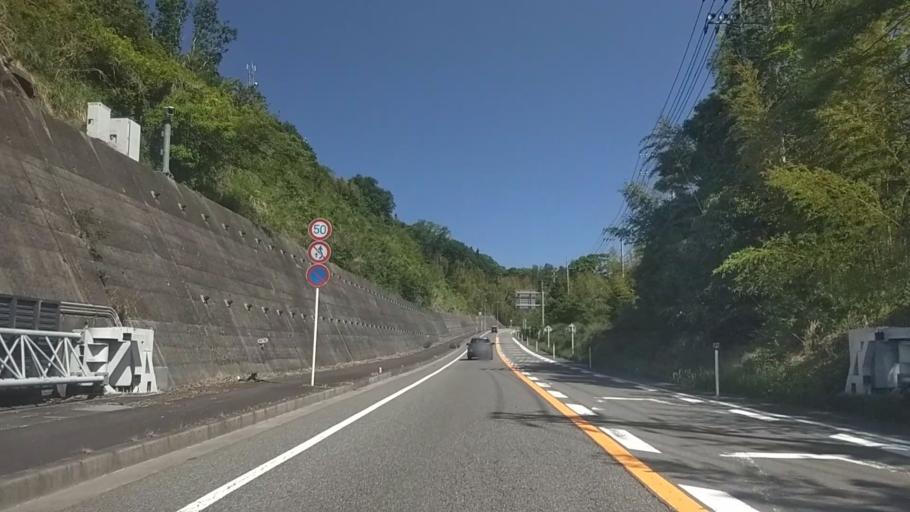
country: JP
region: Shizuoka
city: Fujinomiya
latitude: 35.3836
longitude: 138.4478
